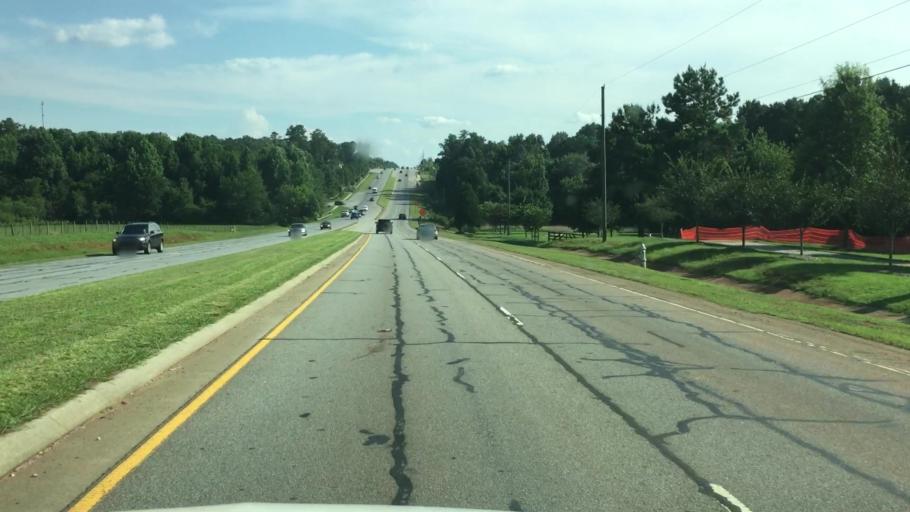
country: US
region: Georgia
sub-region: Gwinnett County
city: Lawrenceville
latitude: 33.9129
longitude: -84.0015
